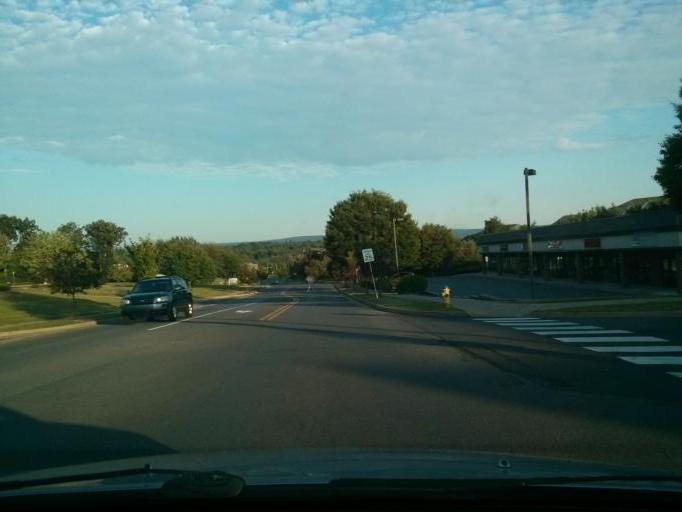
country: US
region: Pennsylvania
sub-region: Centre County
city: Park Forest Village
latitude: 40.8045
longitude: -77.8913
